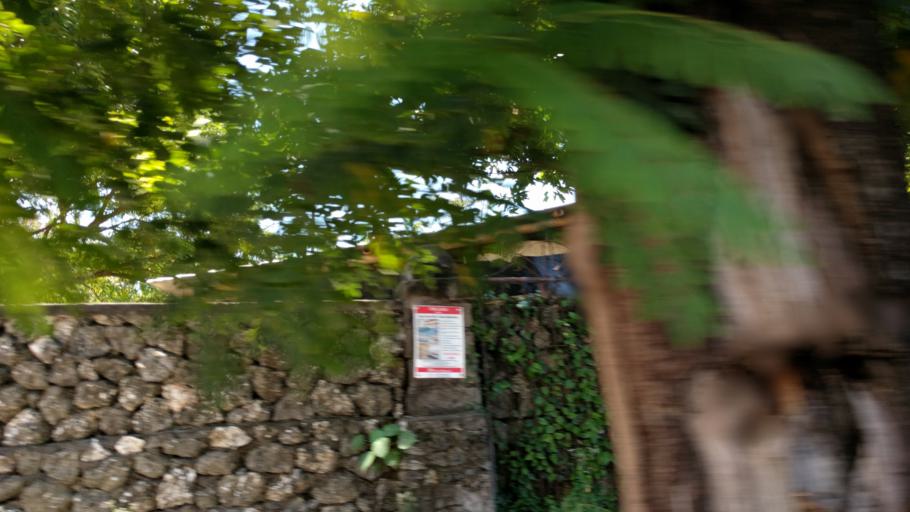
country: ID
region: Bali
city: Banjar Medura
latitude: -8.6984
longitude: 115.2631
